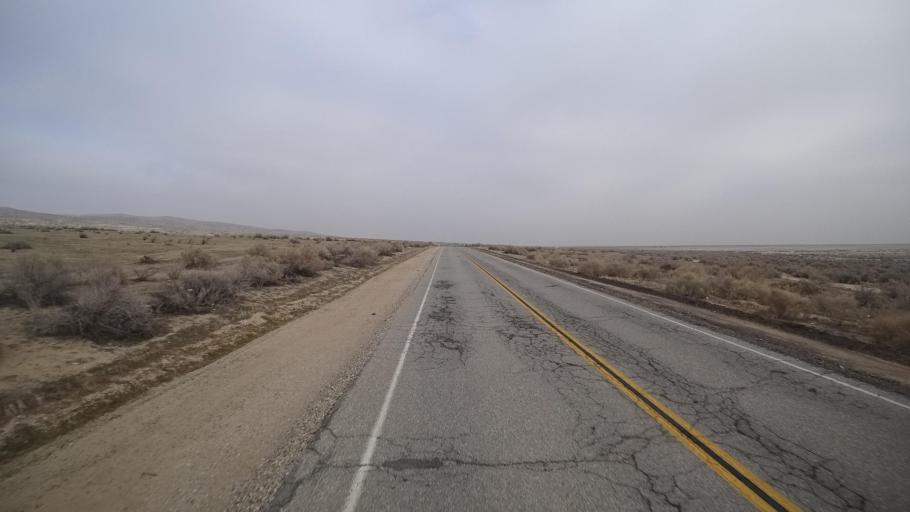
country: US
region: California
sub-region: Kern County
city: South Taft
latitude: 35.1322
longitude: -119.4011
